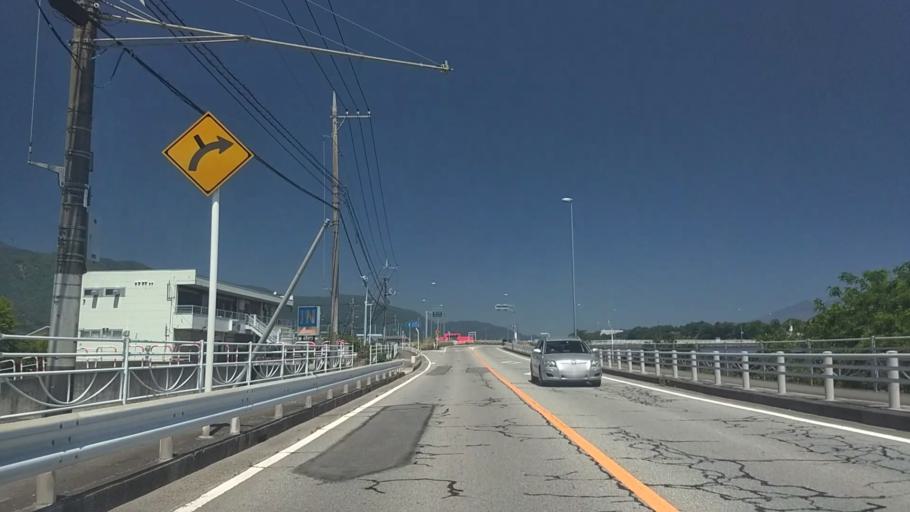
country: JP
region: Yamanashi
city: Nirasaki
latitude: 35.6979
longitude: 138.4548
